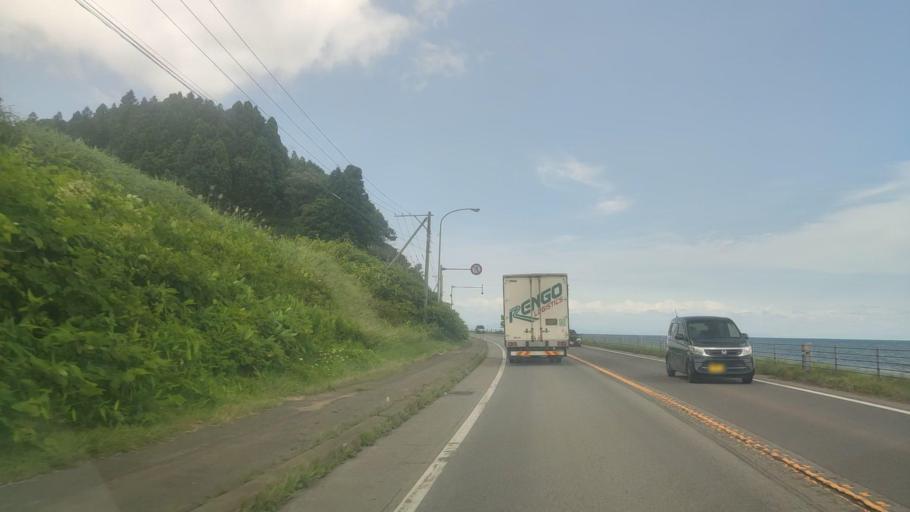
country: JP
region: Hokkaido
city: Nanae
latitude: 42.1463
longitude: 140.4992
